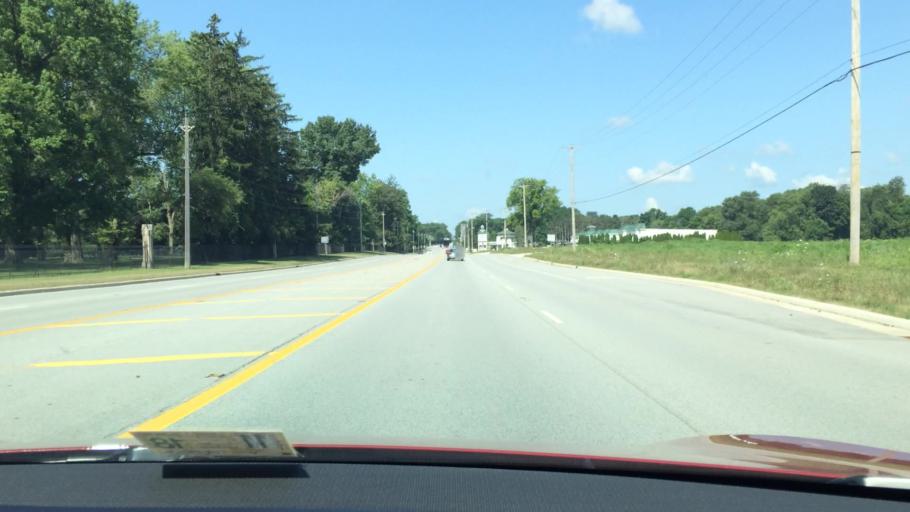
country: US
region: Indiana
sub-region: Saint Joseph County
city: Georgetown
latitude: 41.7240
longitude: -86.1798
